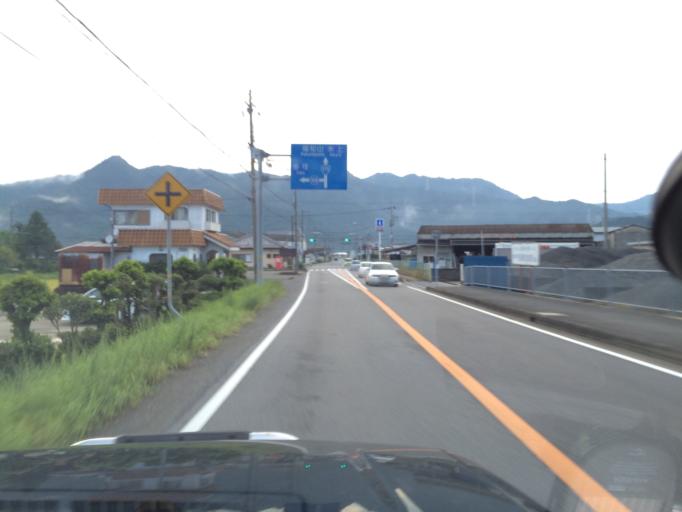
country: JP
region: Hyogo
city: Nishiwaki
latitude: 35.1001
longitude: 134.9966
